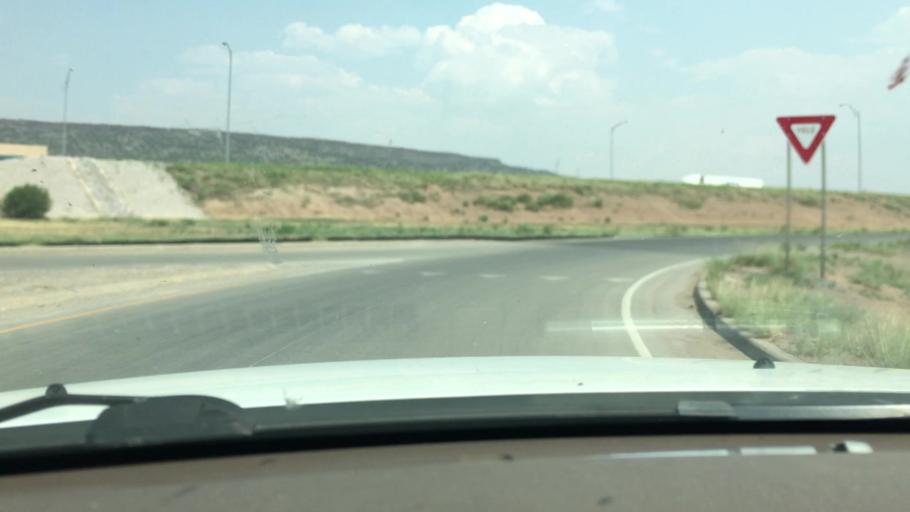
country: US
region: New Mexico
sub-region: Cibola County
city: Milan
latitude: 35.1820
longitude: -107.9025
